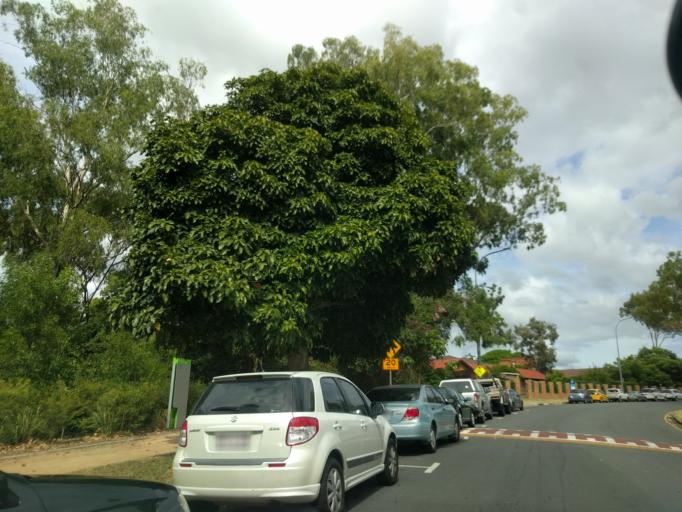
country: AU
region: Queensland
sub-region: Brisbane
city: Yeronga
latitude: -27.5024
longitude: 153.0112
